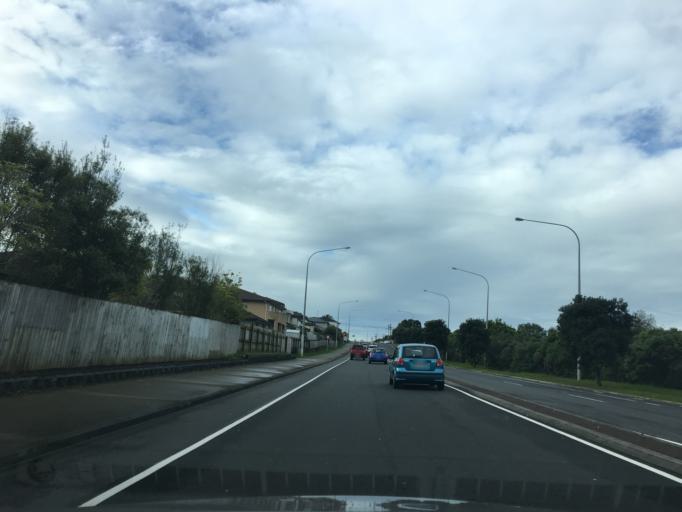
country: NZ
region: Auckland
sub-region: Auckland
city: Rothesay Bay
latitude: -36.7300
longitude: 174.7246
